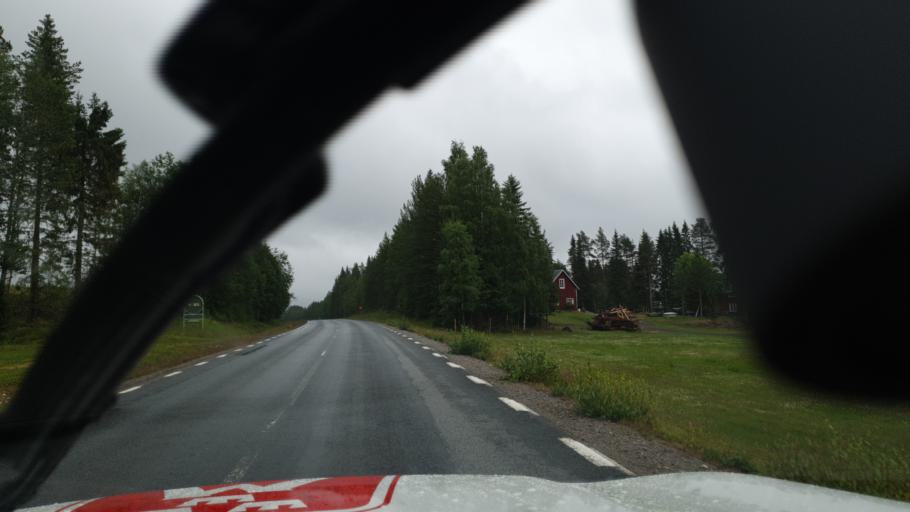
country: SE
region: Vaesterbotten
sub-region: Vannas Kommun
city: Vaennaes
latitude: 63.7725
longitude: 19.6860
